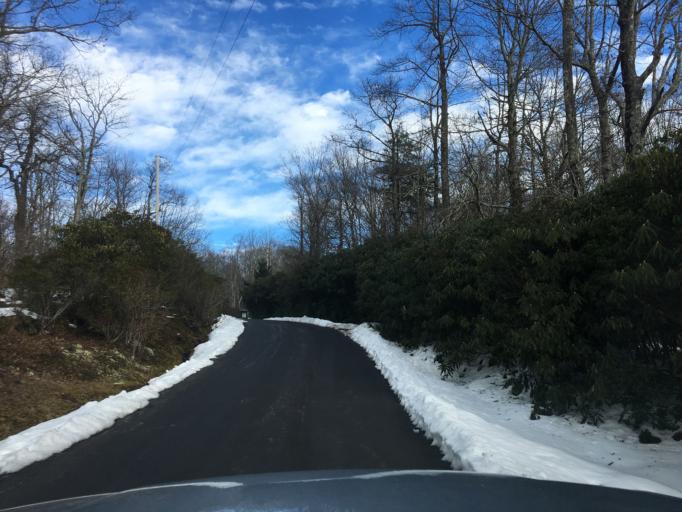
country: US
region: North Carolina
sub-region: Jackson County
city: Cullowhee
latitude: 35.1366
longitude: -82.9966
